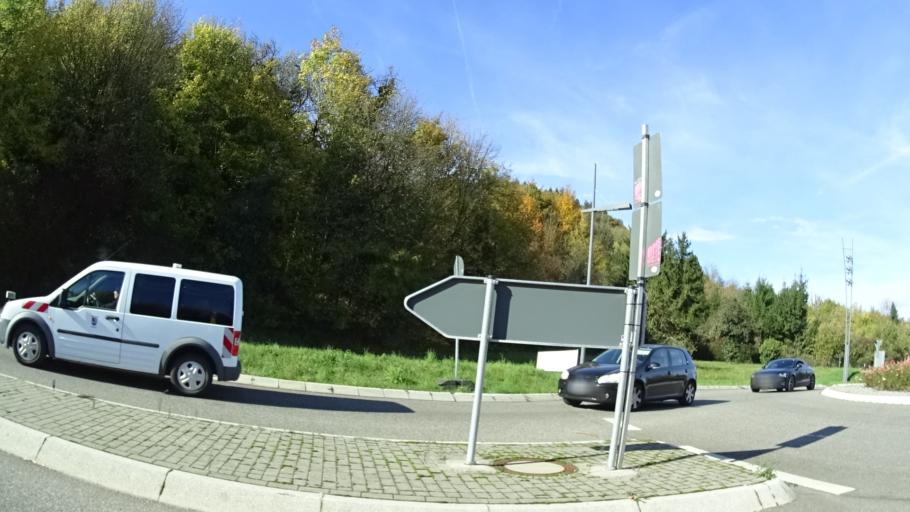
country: DE
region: Baden-Wuerttemberg
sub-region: Karlsruhe Region
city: Joehlingen
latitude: 48.9908
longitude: 8.5346
